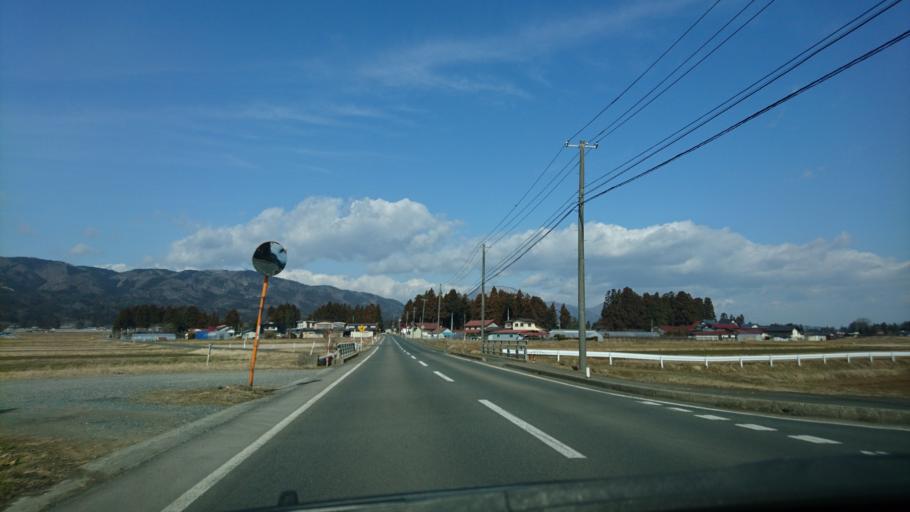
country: JP
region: Iwate
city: Hanamaki
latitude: 39.5213
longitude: 141.1265
